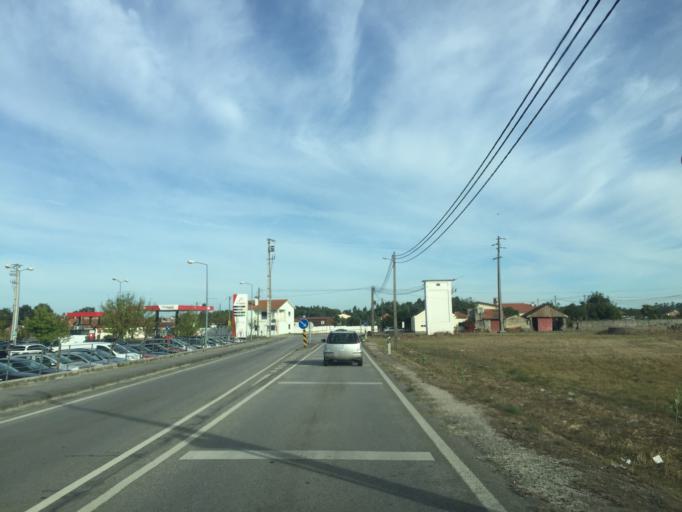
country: PT
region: Leiria
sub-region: Pombal
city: Lourical
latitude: 39.9682
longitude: -8.7923
